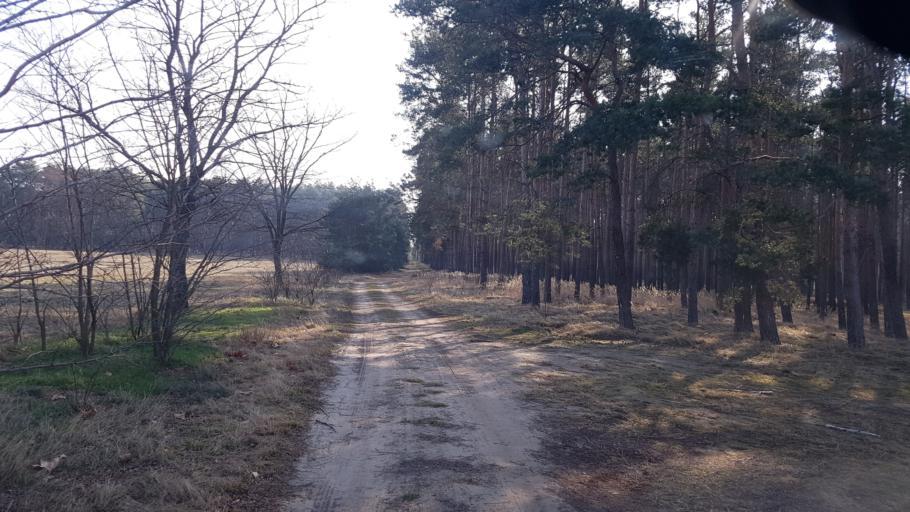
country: DE
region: Brandenburg
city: Schlieben
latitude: 51.6735
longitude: 13.3122
